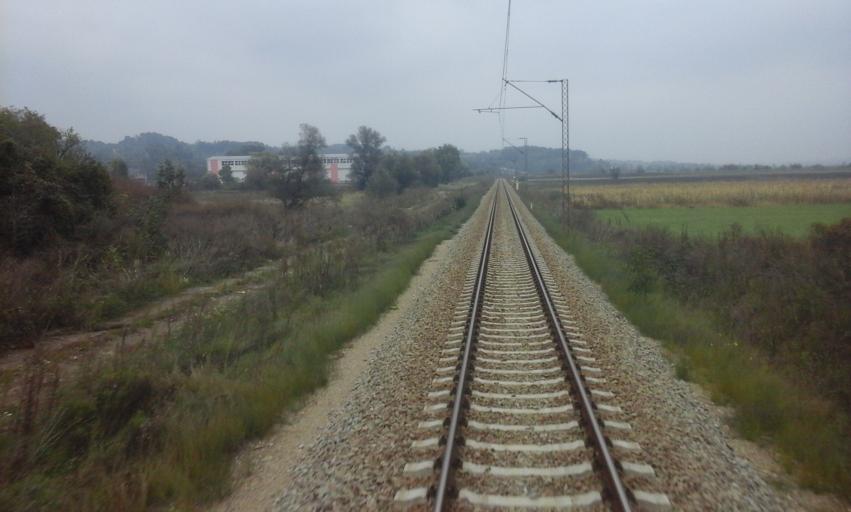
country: RS
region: Central Serbia
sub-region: Belgrade
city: Mladenovac
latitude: 44.4951
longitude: 20.6497
